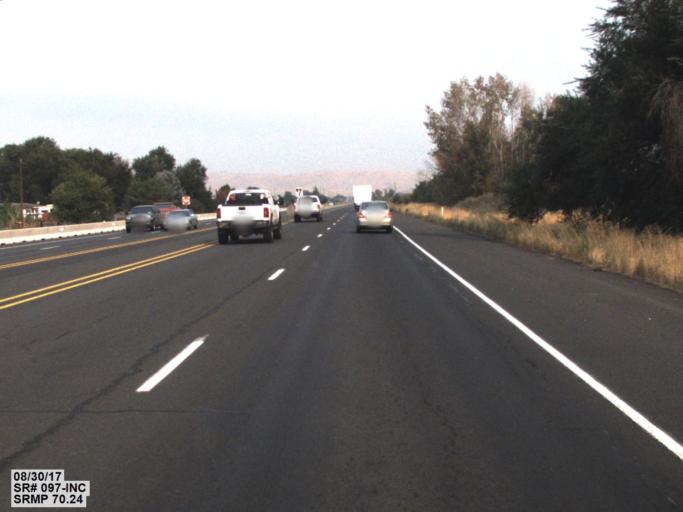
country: US
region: Washington
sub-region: Yakima County
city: Wapato
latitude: 46.4637
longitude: -120.4359
